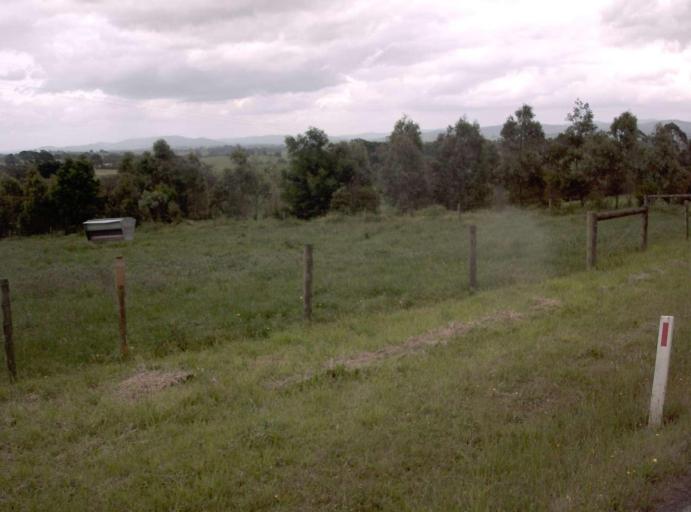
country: AU
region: Victoria
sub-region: Baw Baw
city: Warragul
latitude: -38.0991
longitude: 145.9707
